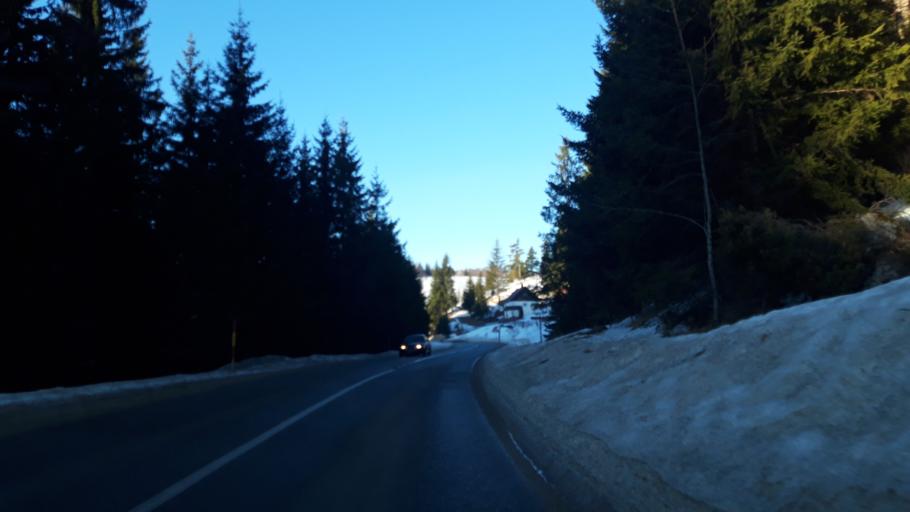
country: BA
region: Republika Srpska
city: Han Pijesak
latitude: 44.1191
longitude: 18.9695
